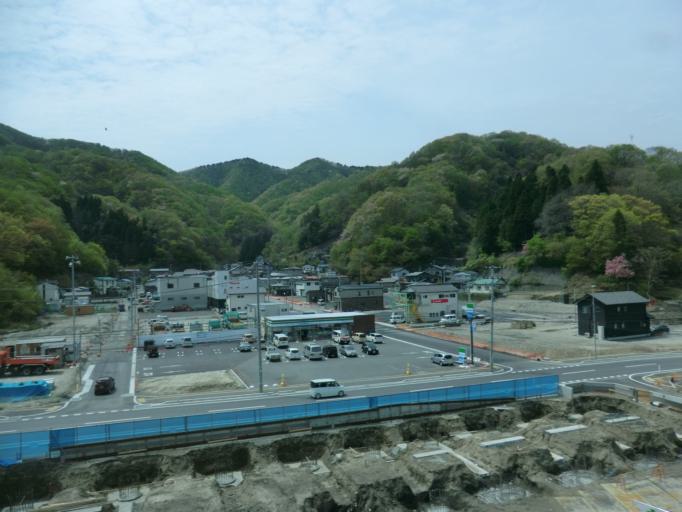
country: JP
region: Iwate
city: Kamaishi
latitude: 39.2670
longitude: 141.8832
